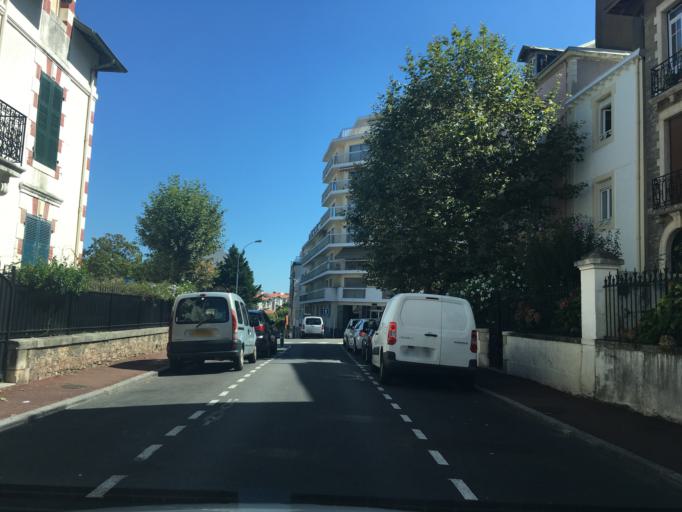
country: FR
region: Aquitaine
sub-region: Departement des Pyrenees-Atlantiques
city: Biarritz
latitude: 43.4802
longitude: -1.5625
